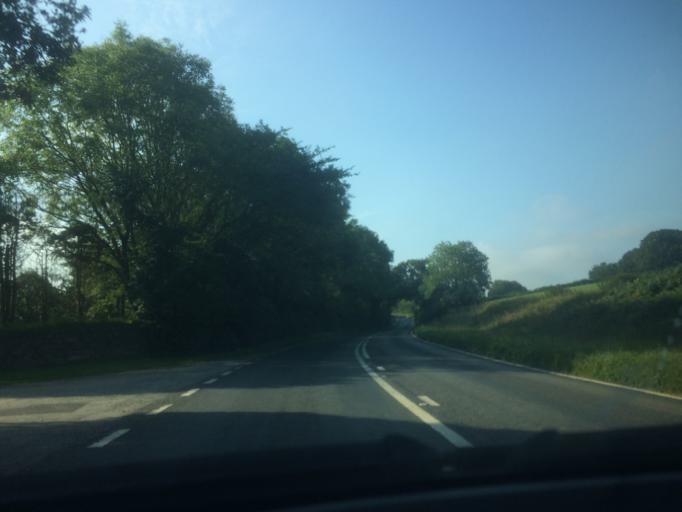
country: GB
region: England
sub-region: Cornwall
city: Pillaton
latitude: 50.4432
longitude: -4.2562
